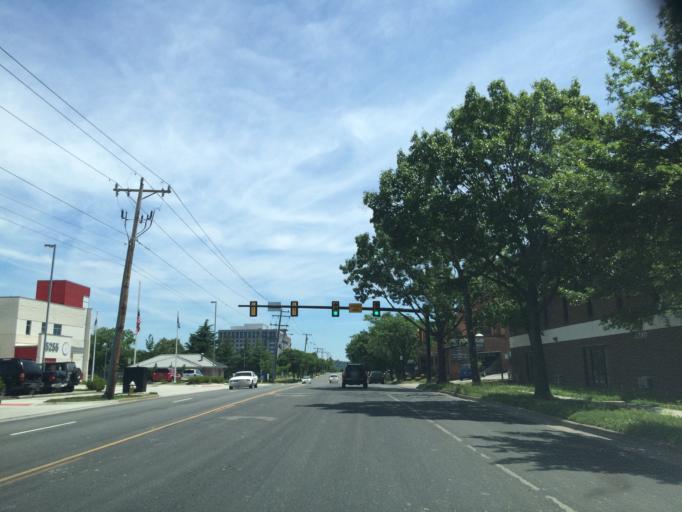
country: US
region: Virginia
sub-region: Fairfax County
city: Rose Hill
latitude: 38.8012
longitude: -77.1273
